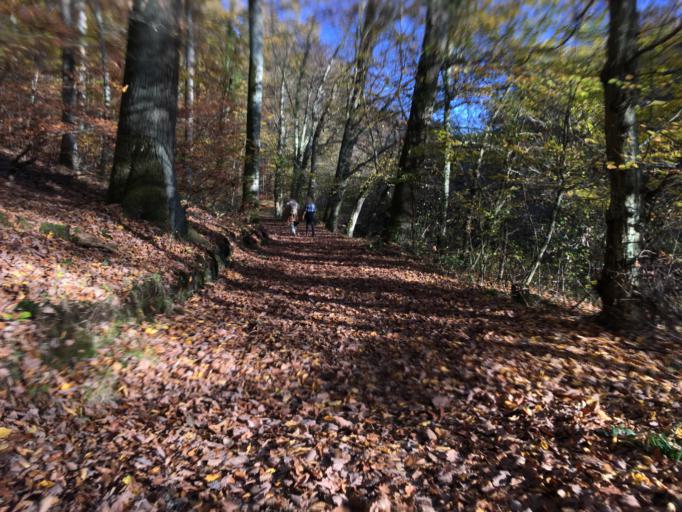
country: DE
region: Baden-Wuerttemberg
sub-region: Karlsruhe Region
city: Sternenfels
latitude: 49.0464
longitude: 8.8378
